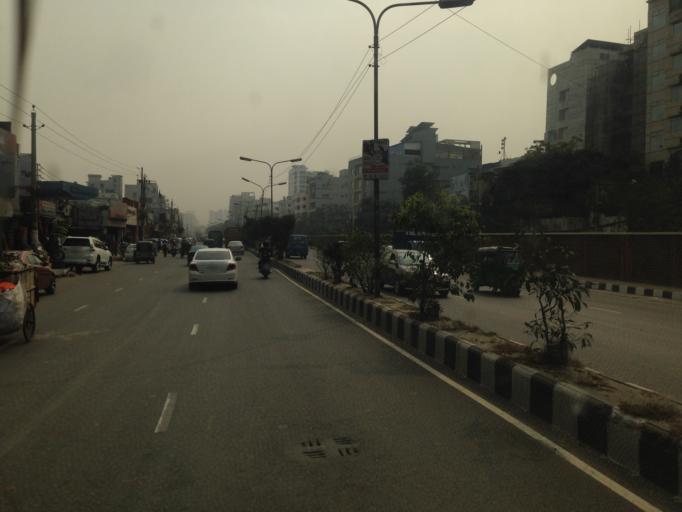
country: BD
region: Dhaka
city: Paltan
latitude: 23.8077
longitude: 90.4216
